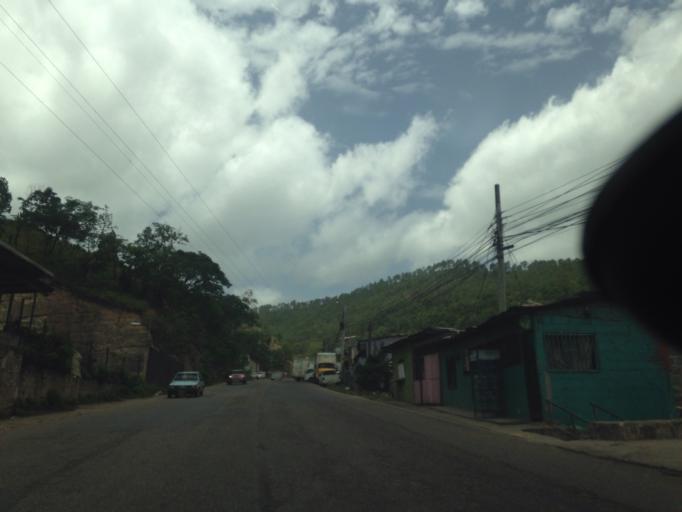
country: HN
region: Francisco Morazan
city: El Tablon
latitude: 14.0522
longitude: -87.1567
